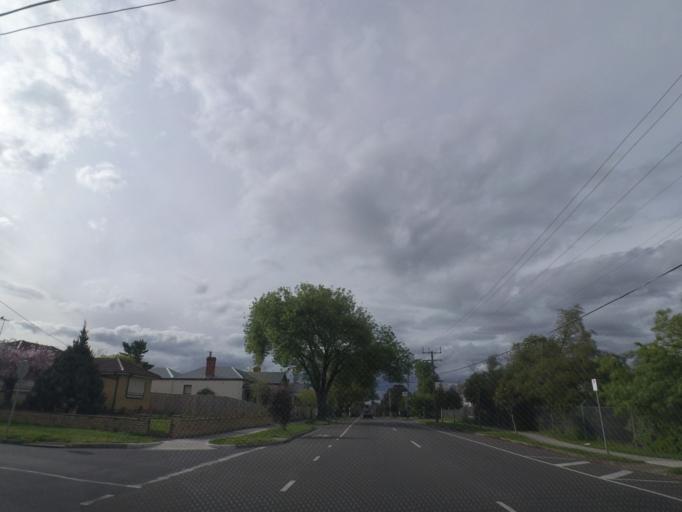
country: AU
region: Victoria
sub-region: Yarra Ranges
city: Lilydale
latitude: -37.7548
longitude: 145.3434
